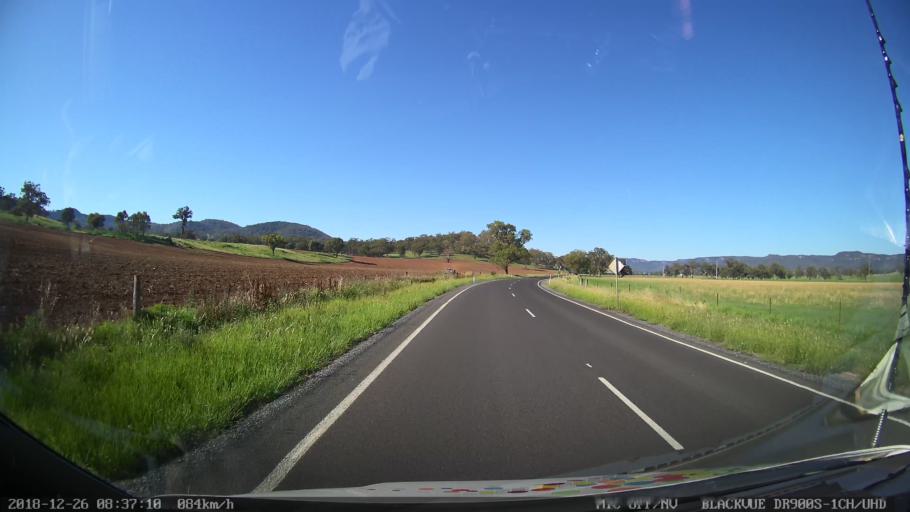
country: AU
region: New South Wales
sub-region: Upper Hunter Shire
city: Merriwa
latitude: -32.4296
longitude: 150.0927
